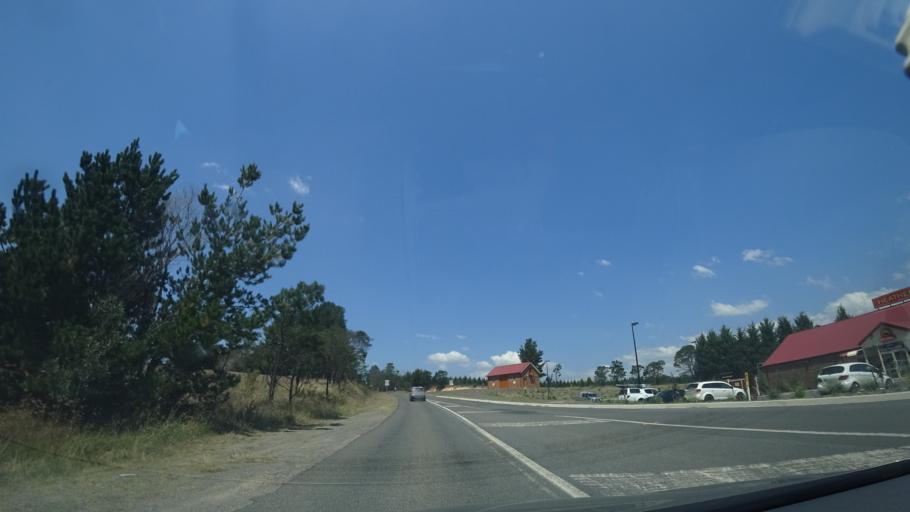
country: AU
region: New South Wales
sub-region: Wingecarribee
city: Bundanoon
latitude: -34.6087
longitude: 150.2302
